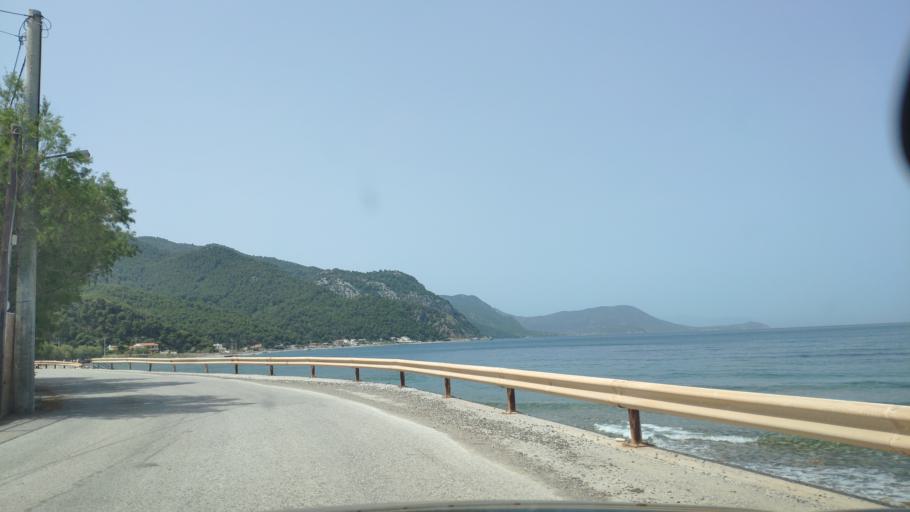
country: GR
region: Attica
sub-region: Nomarchia Dytikis Attikis
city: Kineta
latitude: 38.0703
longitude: 23.1510
